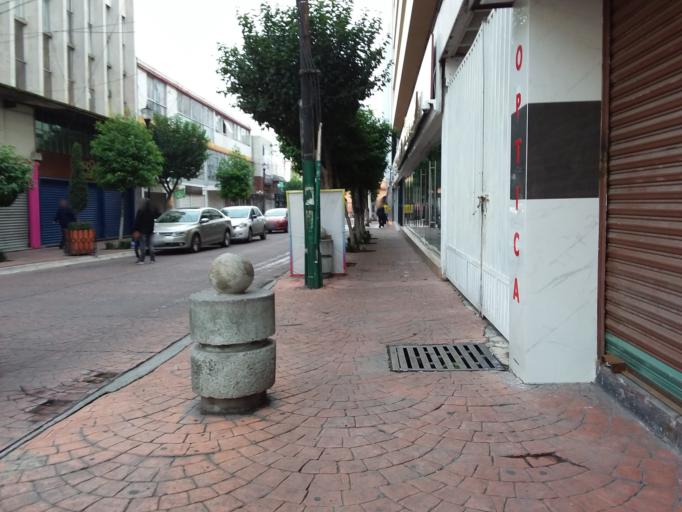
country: MX
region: Mexico
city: Toluca
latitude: 19.2894
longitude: -99.6557
